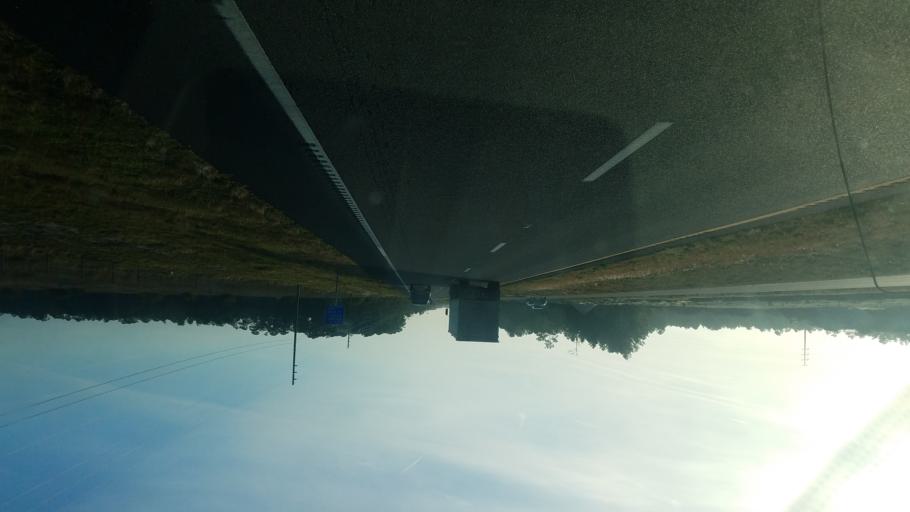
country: US
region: Florida
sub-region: Osceola County
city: Saint Cloud
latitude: 28.2244
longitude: -81.1818
